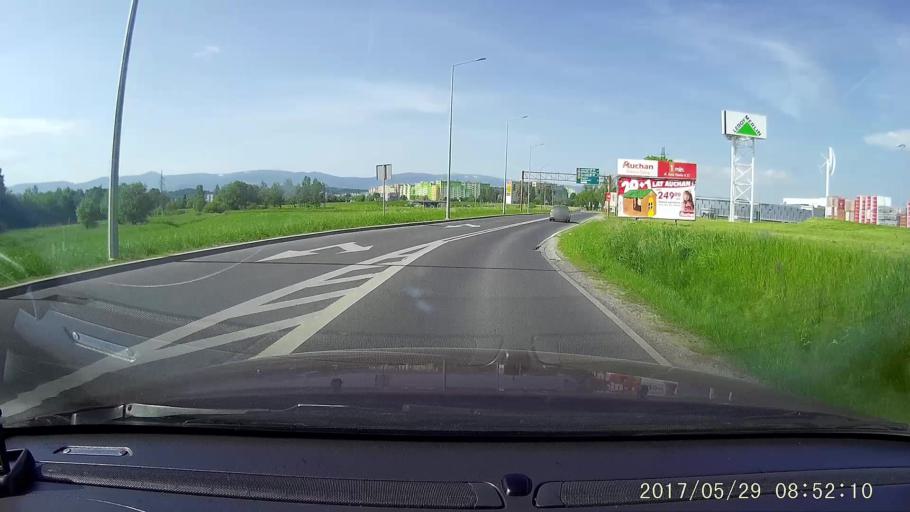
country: PL
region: Lower Silesian Voivodeship
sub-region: Powiat jeleniogorski
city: Jezow Sudecki
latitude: 50.9233
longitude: 15.7680
